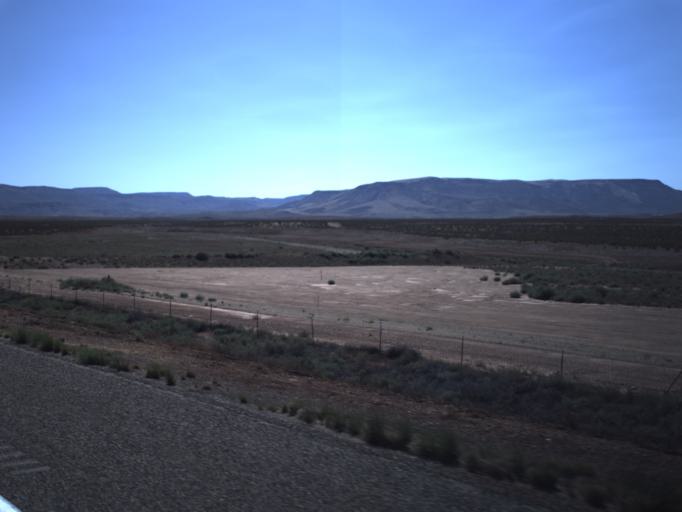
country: US
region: Utah
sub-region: Washington County
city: Saint George
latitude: 37.0172
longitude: -113.5963
